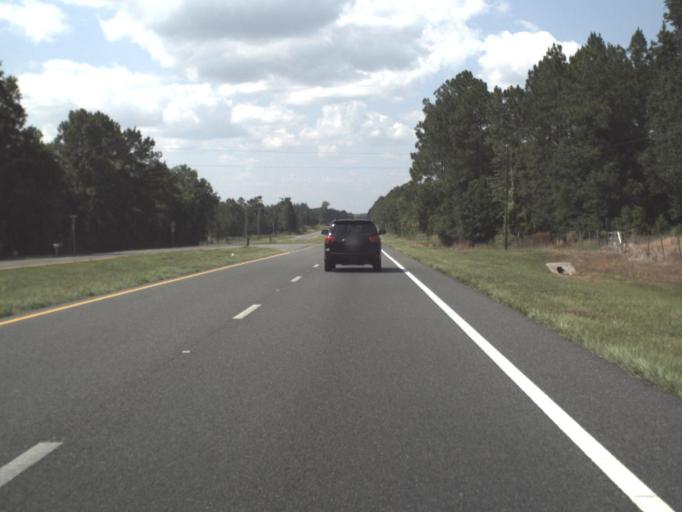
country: US
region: Florida
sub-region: Alachua County
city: Waldo
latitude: 29.7296
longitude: -82.1410
